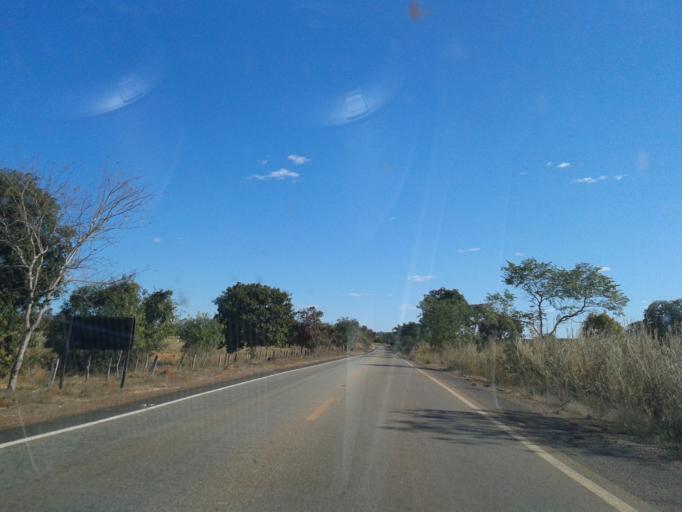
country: BR
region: Goias
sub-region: Mozarlandia
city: Mozarlandia
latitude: -14.6552
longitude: -50.5252
